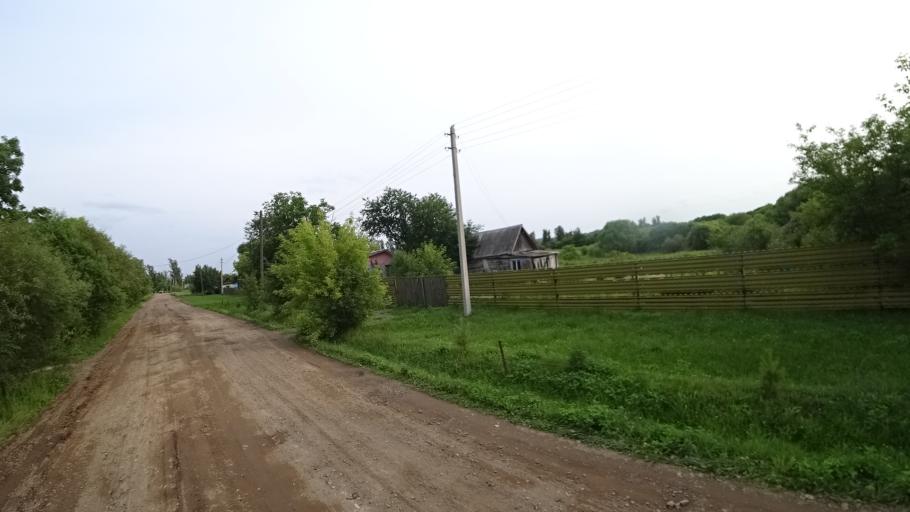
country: RU
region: Primorskiy
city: Novosysoyevka
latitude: 44.2499
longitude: 133.3766
